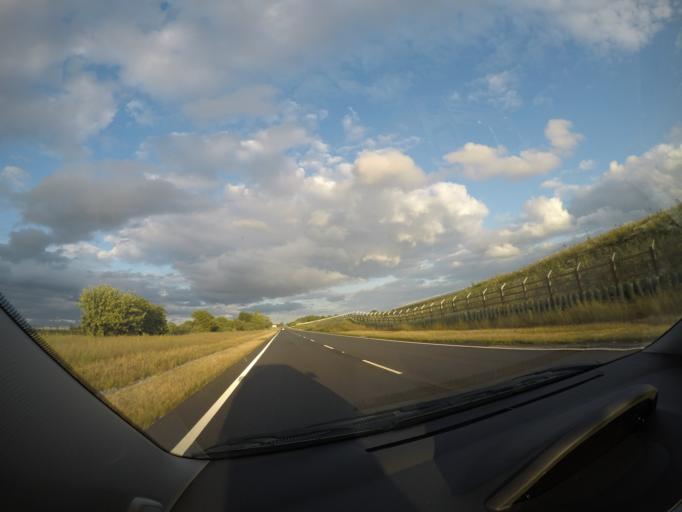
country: GB
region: England
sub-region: North Yorkshire
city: Catterick
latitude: 54.3736
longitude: -1.6397
